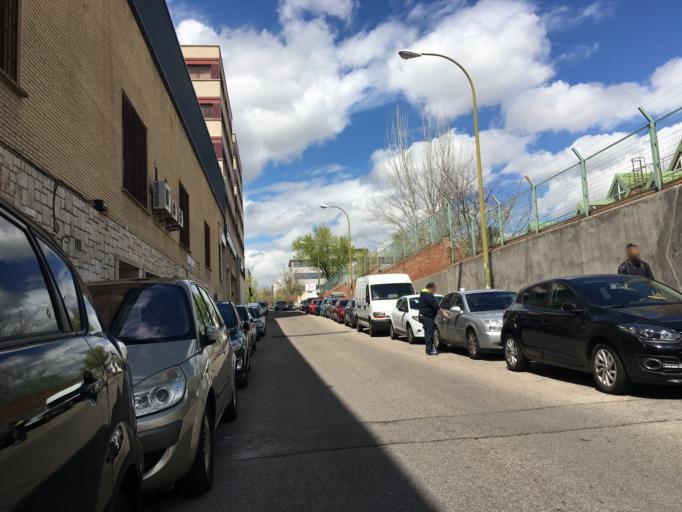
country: ES
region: Madrid
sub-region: Provincia de Madrid
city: San Blas
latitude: 40.4344
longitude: -3.6262
